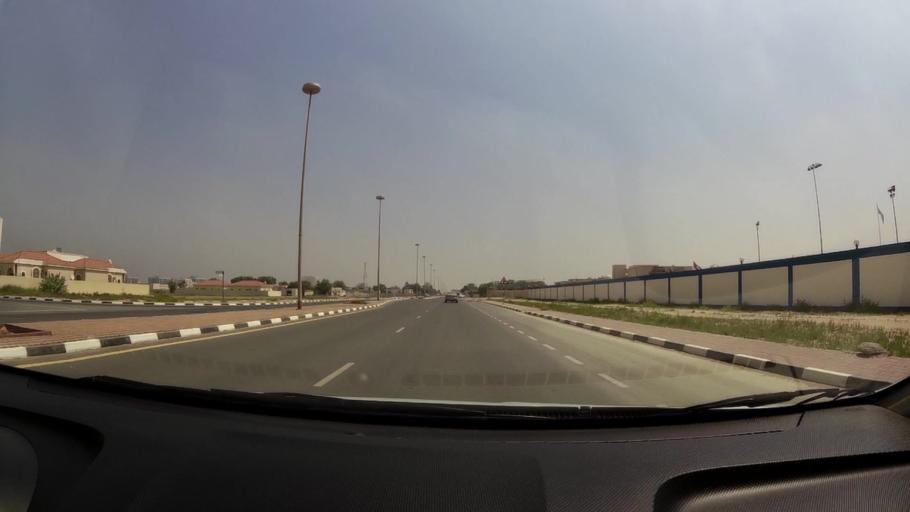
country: AE
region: Umm al Qaywayn
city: Umm al Qaywayn
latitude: 25.5682
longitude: 55.5589
